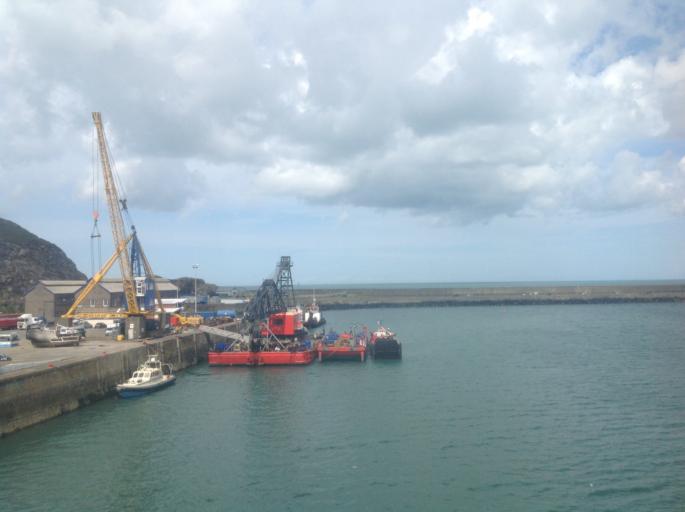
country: GB
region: Wales
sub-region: Pembrokeshire
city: Goodwick
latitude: 52.0114
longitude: -4.9848
